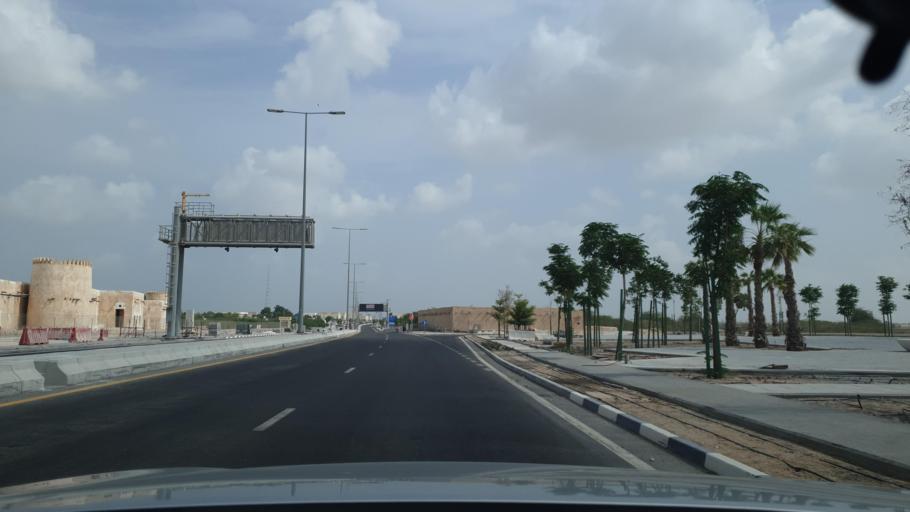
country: QA
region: Baladiyat ar Rayyan
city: Ar Rayyan
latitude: 25.2764
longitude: 51.4501
